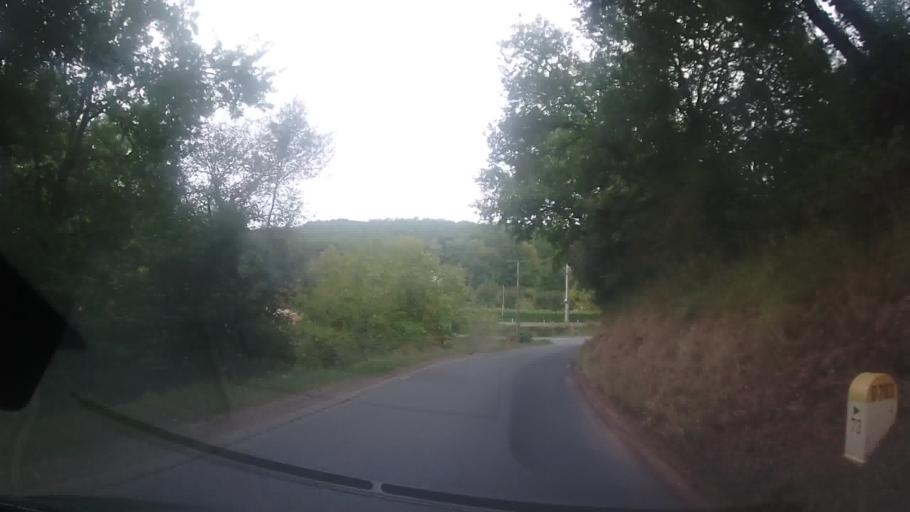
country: FR
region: Aquitaine
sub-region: Departement de la Dordogne
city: Carsac-Aillac
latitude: 44.8454
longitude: 1.2552
